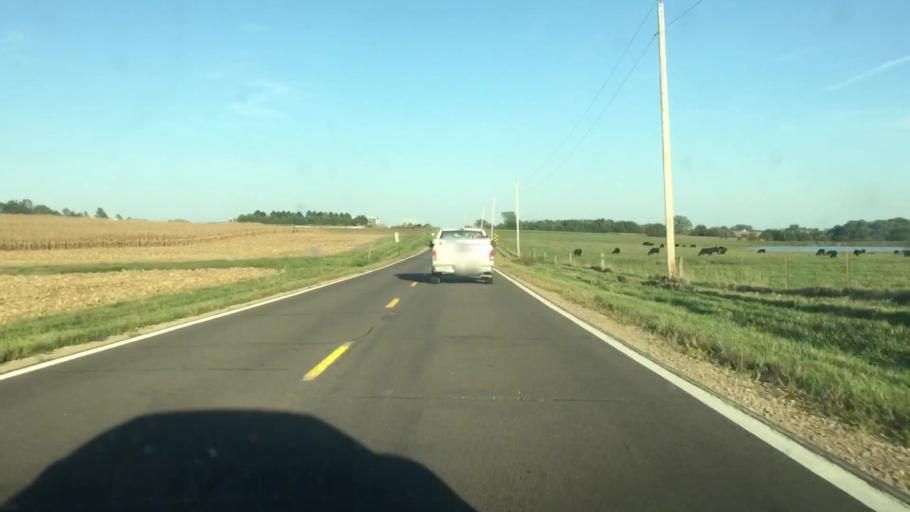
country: US
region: Kansas
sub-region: Brown County
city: Horton
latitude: 39.5512
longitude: -95.4170
